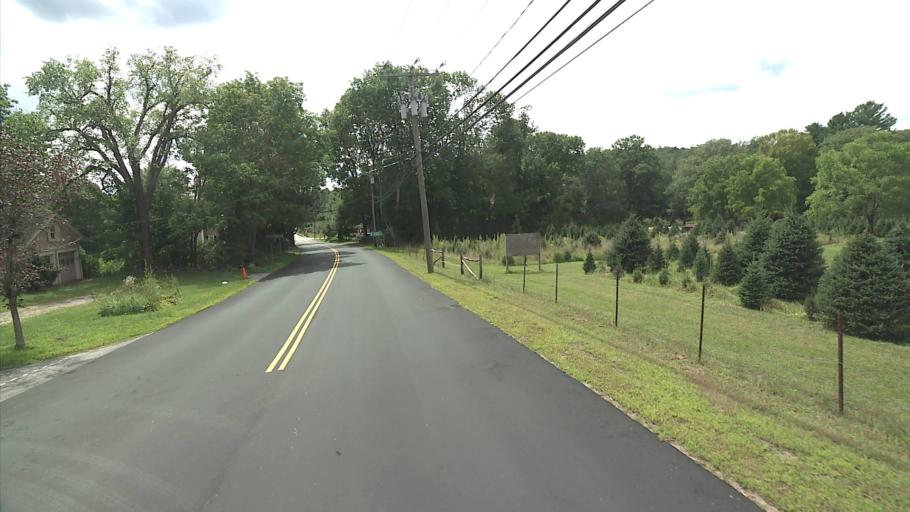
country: US
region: Connecticut
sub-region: Windham County
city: South Woodstock
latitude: 41.9412
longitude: -72.0722
